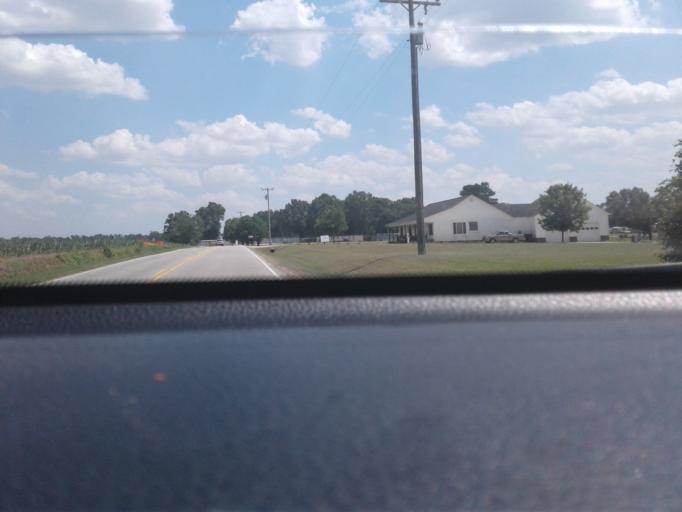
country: US
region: North Carolina
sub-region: Harnett County
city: Erwin
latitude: 35.2978
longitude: -78.6669
